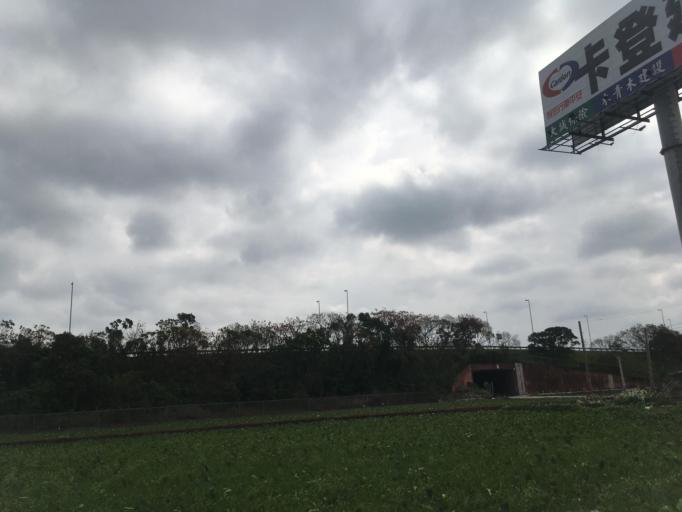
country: TW
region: Taiwan
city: Fengyuan
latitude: 24.4008
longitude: 120.6688
